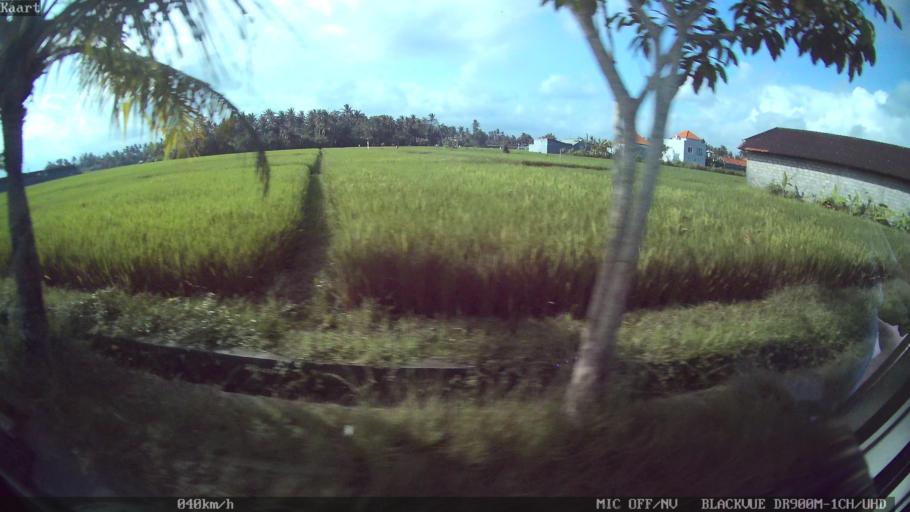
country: ID
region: Bali
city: Banjar Bucu
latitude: -8.5780
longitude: 115.2015
